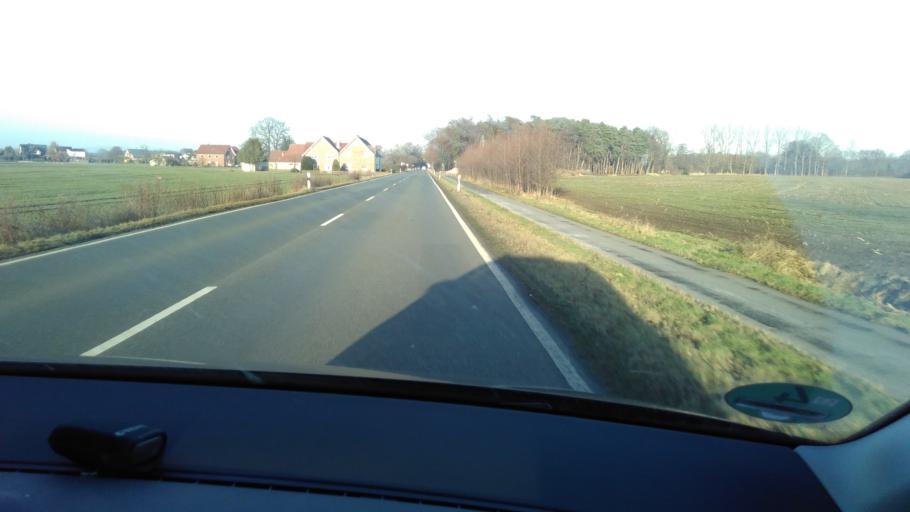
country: DE
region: North Rhine-Westphalia
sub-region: Regierungsbezirk Detmold
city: Verl
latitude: 51.8891
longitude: 8.5190
